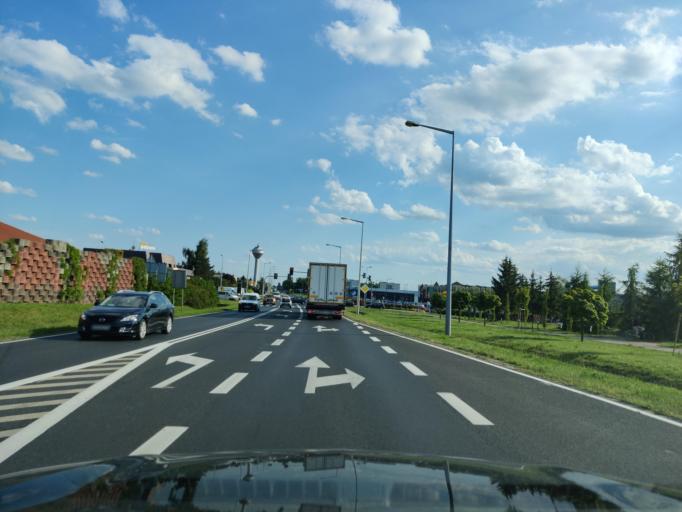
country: PL
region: Greater Poland Voivodeship
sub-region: Powiat wolsztynski
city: Wolsztyn
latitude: 52.1192
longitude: 16.1275
